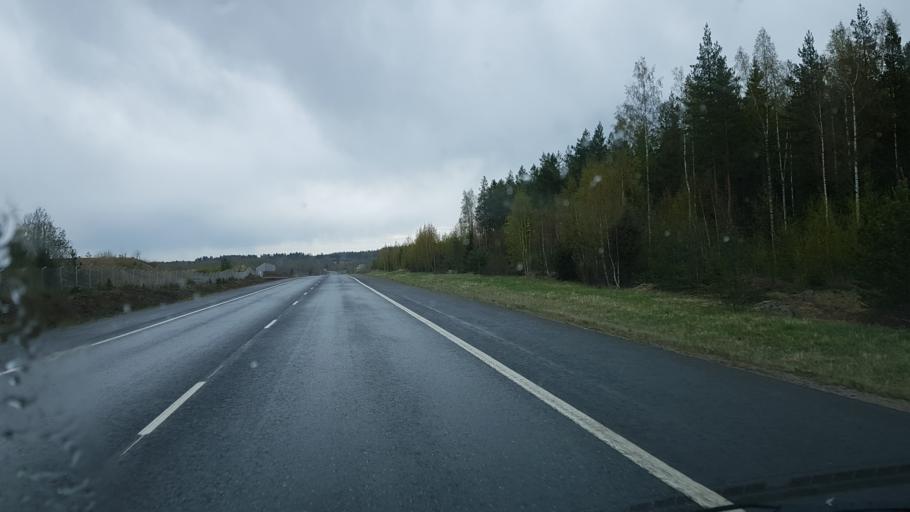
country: FI
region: Pirkanmaa
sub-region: Tampere
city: Pirkkala
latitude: 61.4152
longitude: 23.6343
